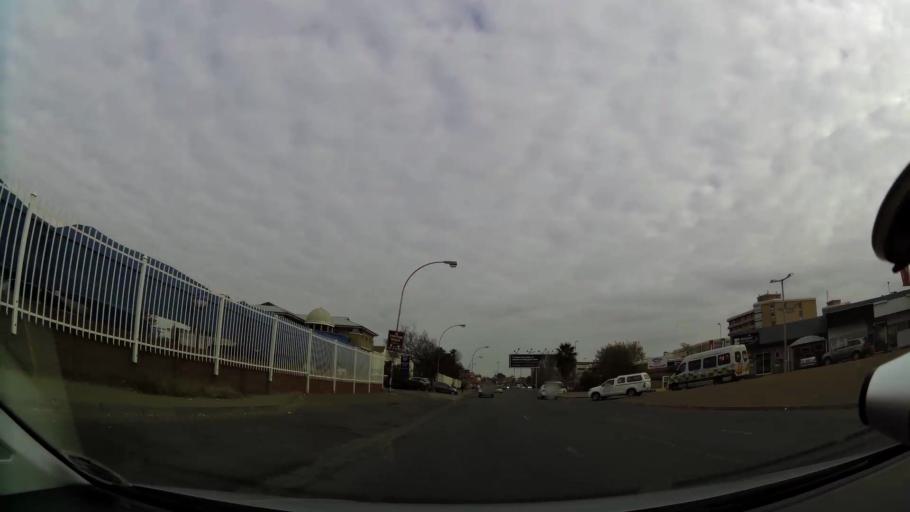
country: ZA
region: Orange Free State
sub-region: Mangaung Metropolitan Municipality
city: Bloemfontein
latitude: -29.1108
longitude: 26.2047
